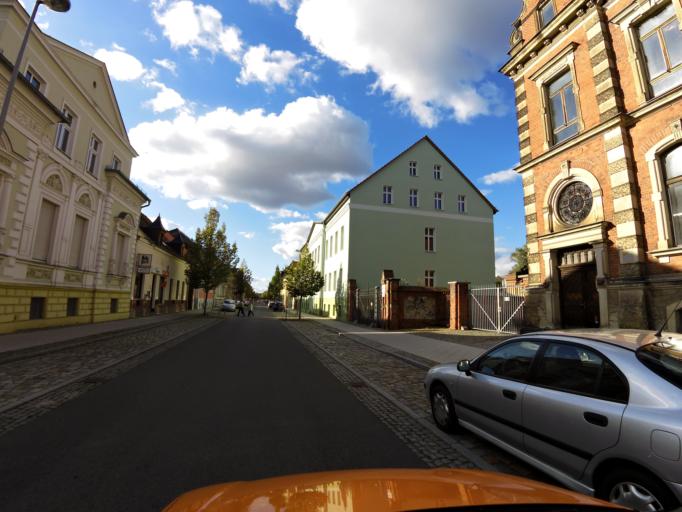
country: DE
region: Brandenburg
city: Luckenwalde
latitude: 52.0902
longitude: 13.1707
